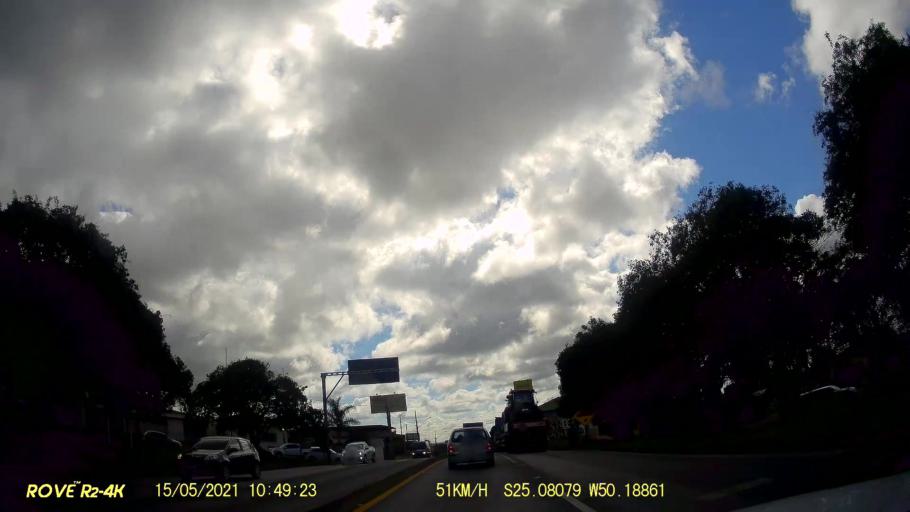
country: BR
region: Parana
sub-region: Ponta Grossa
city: Ponta Grossa
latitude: -25.0804
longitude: -50.1885
